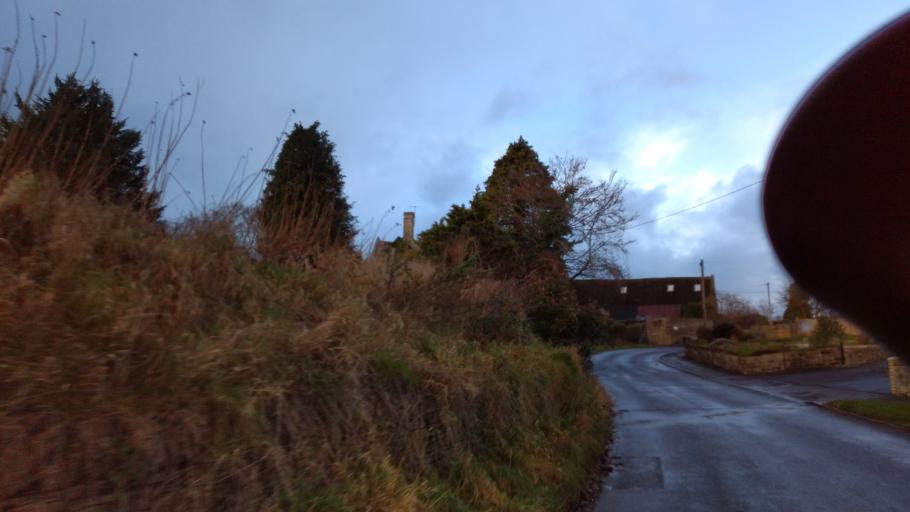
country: GB
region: England
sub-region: Wiltshire
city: Atworth
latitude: 51.3944
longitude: -2.1681
